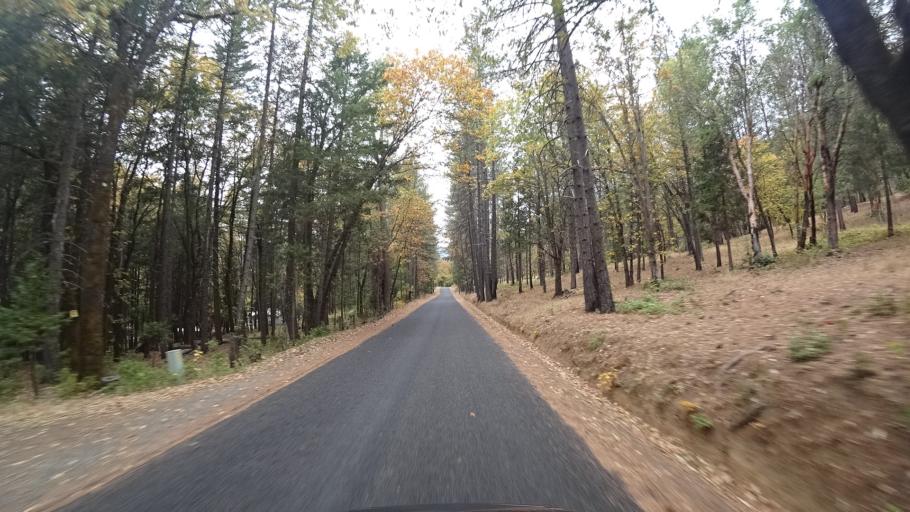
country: US
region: California
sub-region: Siskiyou County
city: Happy Camp
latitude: 41.8600
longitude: -123.1567
